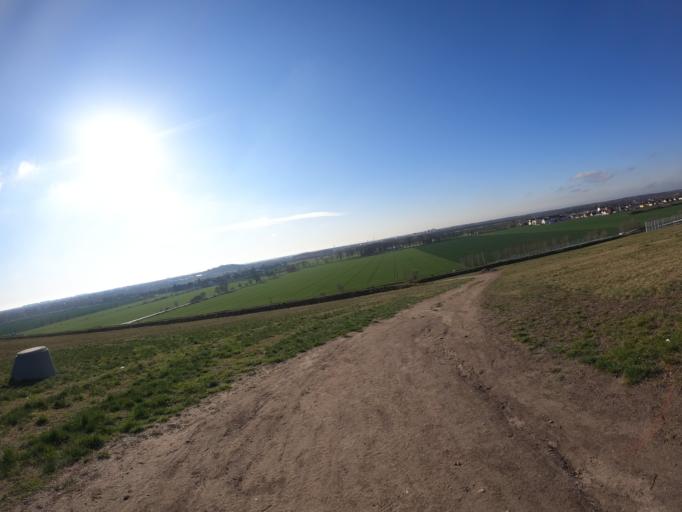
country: DE
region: Berlin
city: Gropiusstadt
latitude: 52.4096
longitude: 13.4581
